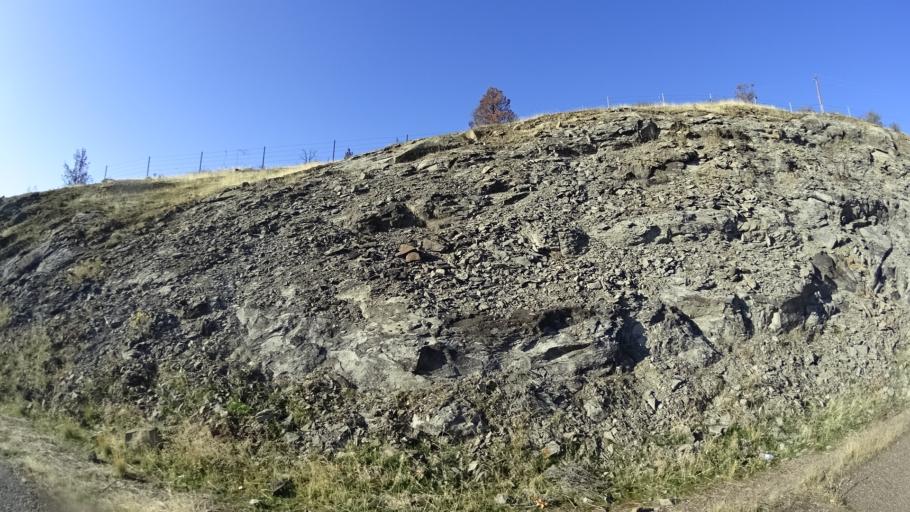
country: US
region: California
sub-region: Siskiyou County
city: Yreka
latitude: 41.9035
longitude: -122.5696
